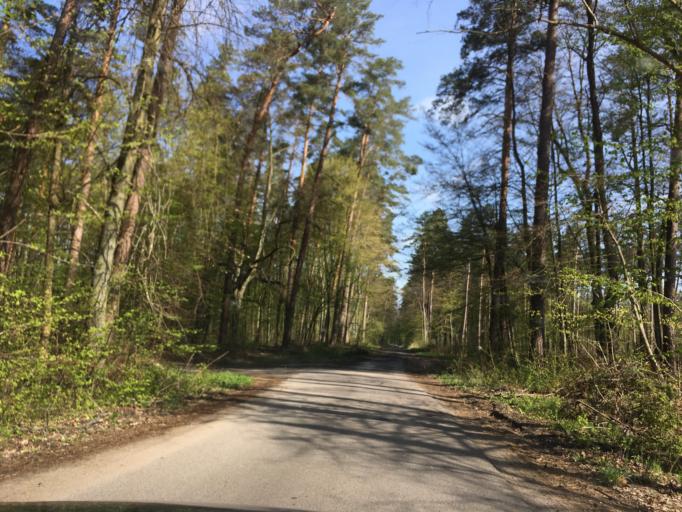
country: PL
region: Warmian-Masurian Voivodeship
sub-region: Powiat piski
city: Ruciane-Nida
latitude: 53.6869
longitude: 21.5890
